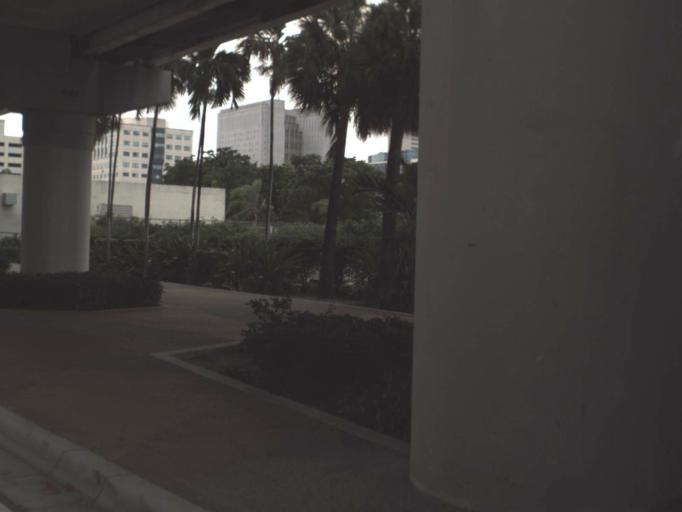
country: US
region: Florida
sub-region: Miami-Dade County
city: Miami
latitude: 25.7826
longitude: -80.1906
